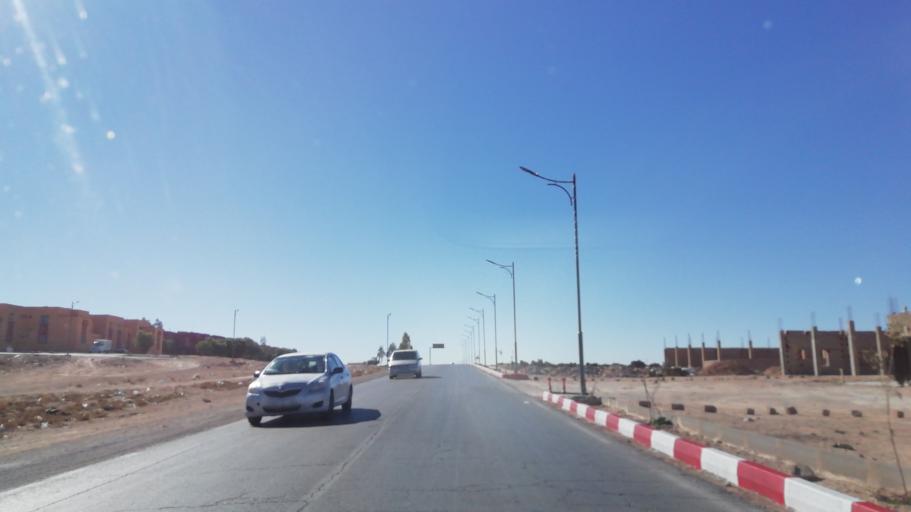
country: DZ
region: Saida
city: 'Ain el Hadjar
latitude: 34.0370
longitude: 0.0786
